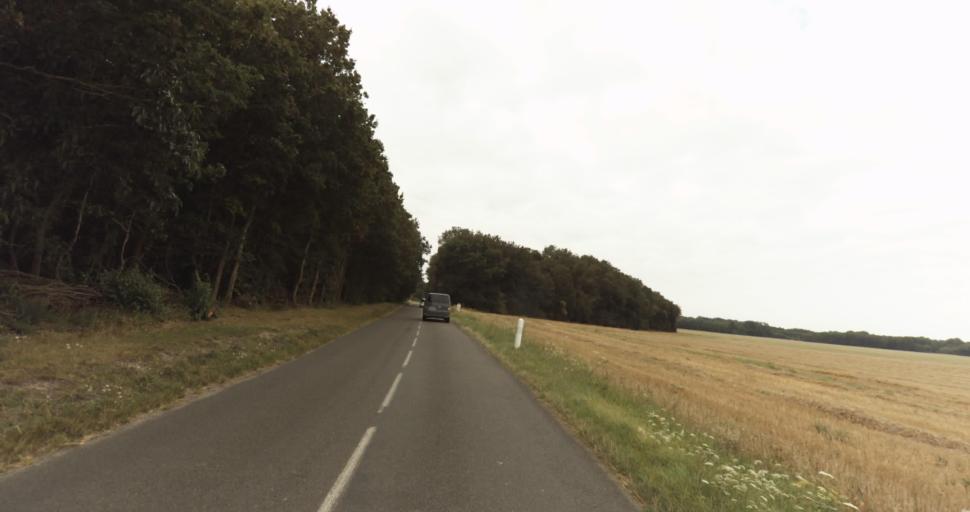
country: FR
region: Haute-Normandie
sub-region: Departement de l'Eure
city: Marcilly-sur-Eure
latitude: 48.8205
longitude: 1.3085
